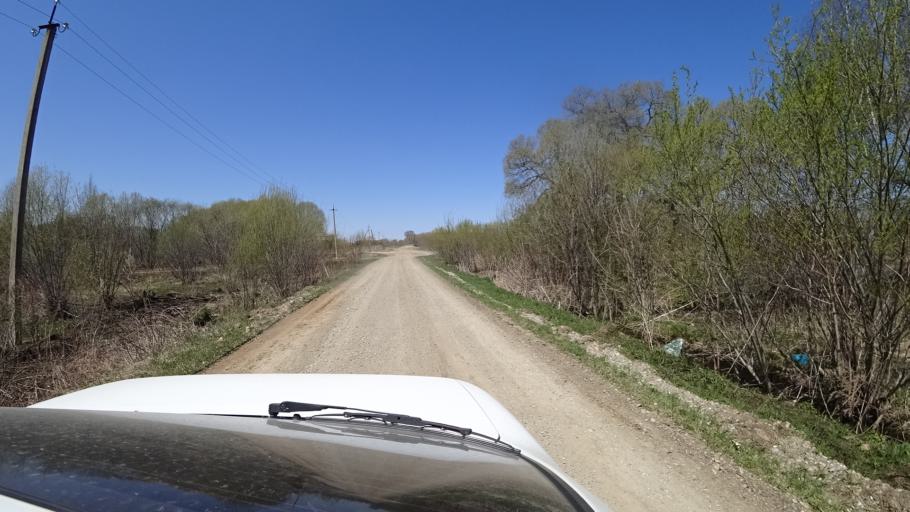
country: RU
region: Primorskiy
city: Lazo
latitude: 45.7952
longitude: 133.7629
